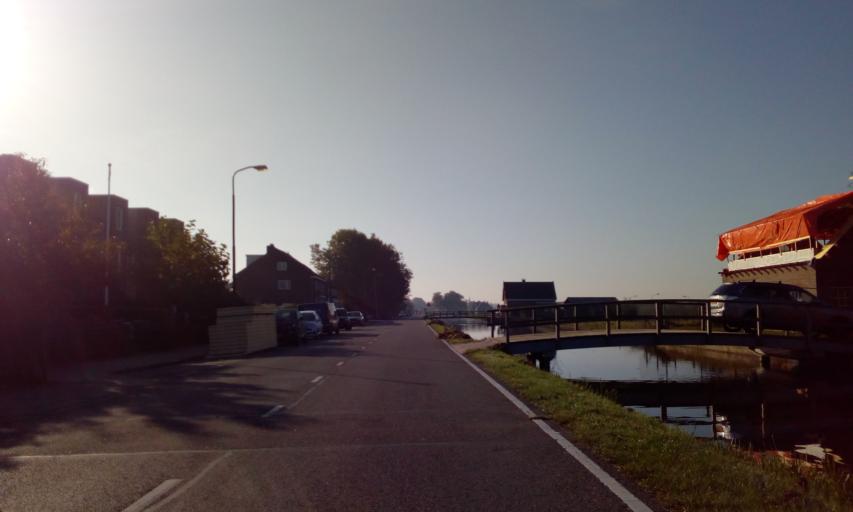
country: NL
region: South Holland
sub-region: Gemeente Lansingerland
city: Berkel en Rodenrijs
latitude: 52.0048
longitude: 4.4830
